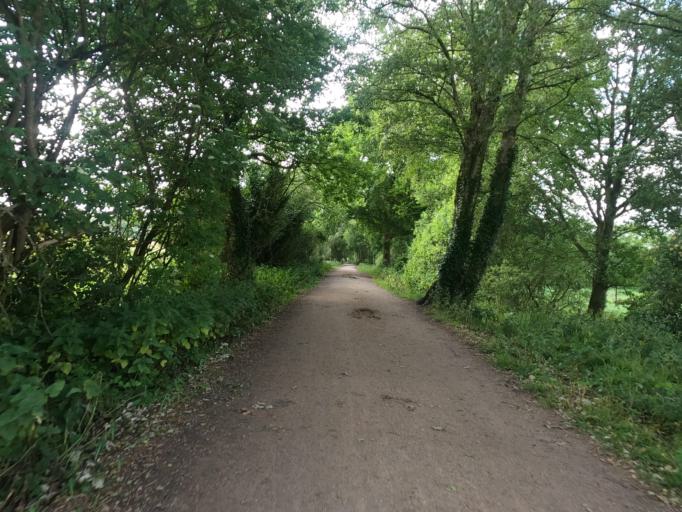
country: GB
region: England
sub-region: Cheshire West and Chester
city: Cuddington
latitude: 53.2081
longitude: -2.5795
